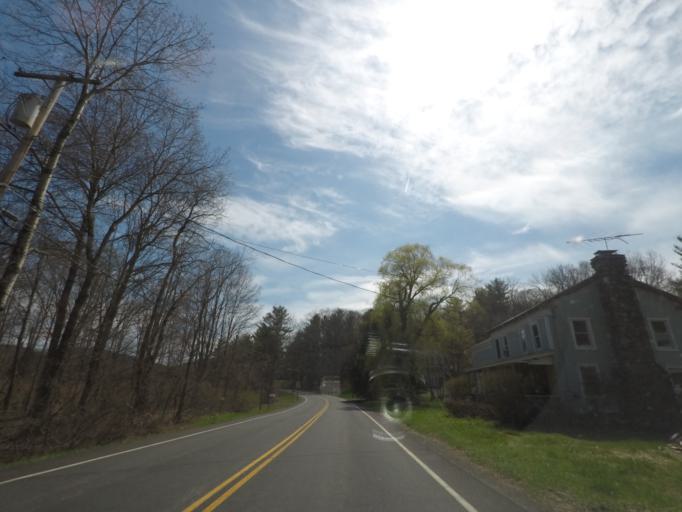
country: US
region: New York
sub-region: Columbia County
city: Chatham
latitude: 42.3900
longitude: -73.5297
